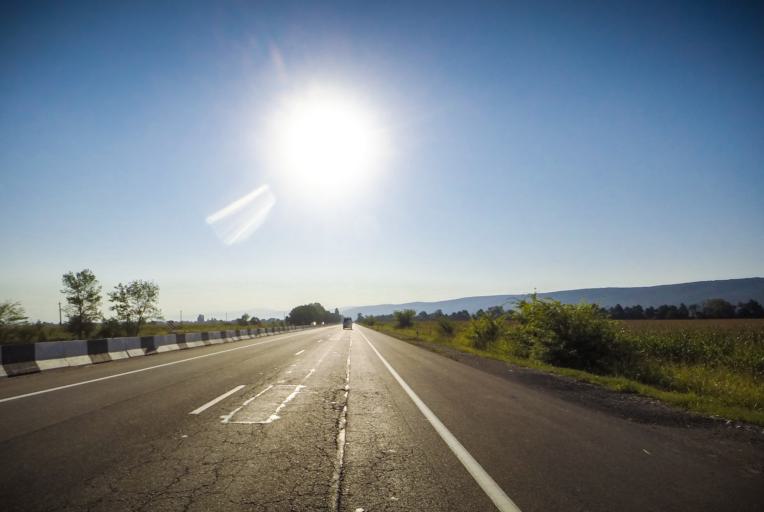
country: RU
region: North Ossetia
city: Zmeyskaya
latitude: 43.3228
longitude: 44.1156
